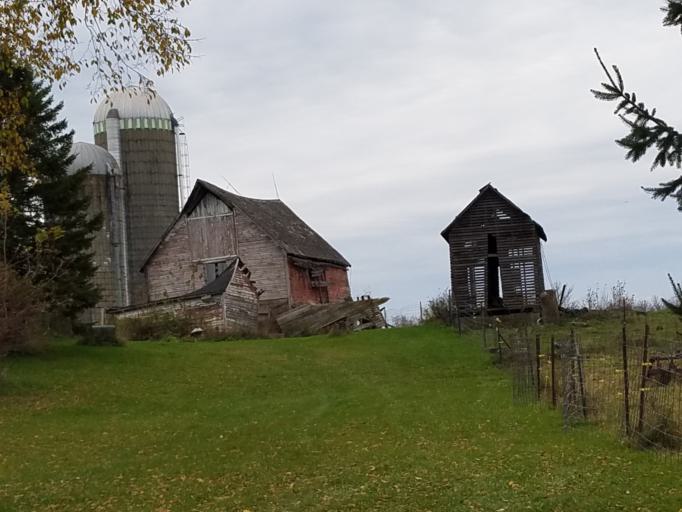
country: US
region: Wisconsin
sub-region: Vernon County
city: Hillsboro
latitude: 43.6290
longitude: -90.2979
